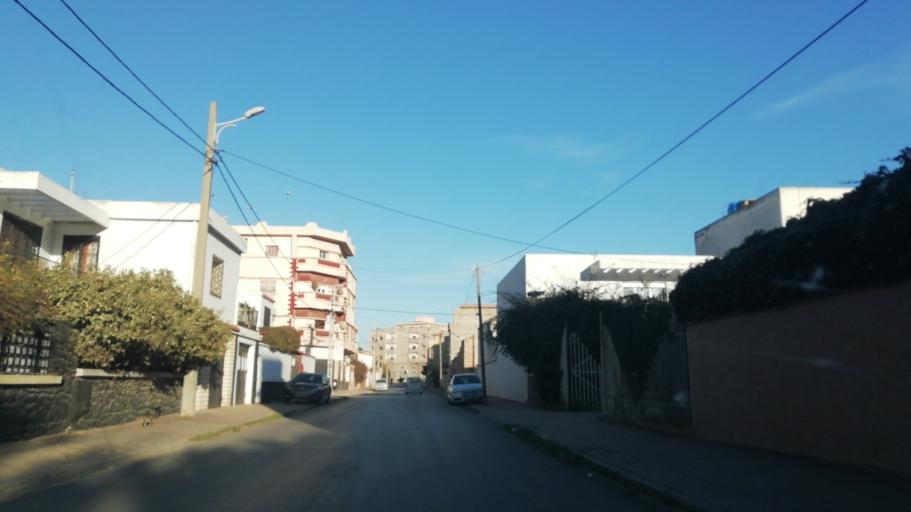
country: DZ
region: Oran
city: Oran
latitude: 35.7084
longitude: -0.6070
